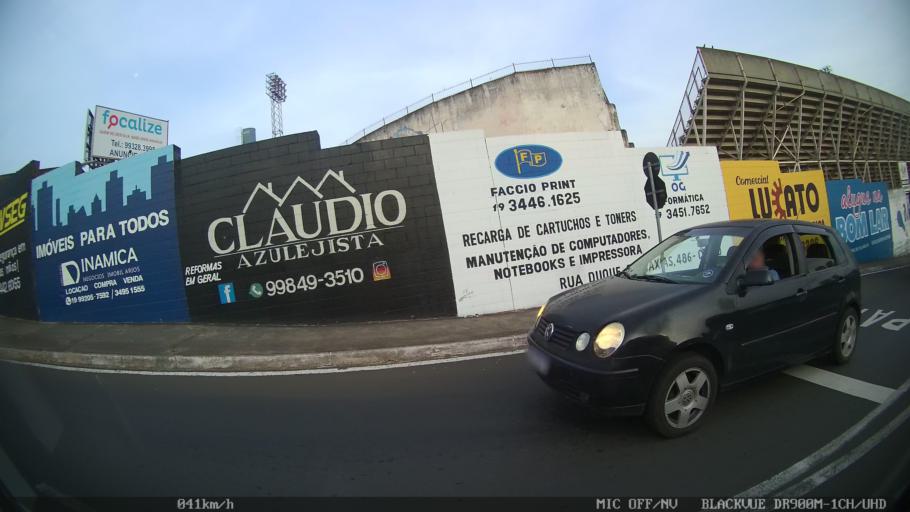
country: BR
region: Sao Paulo
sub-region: Limeira
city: Limeira
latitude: -22.5741
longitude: -47.4134
